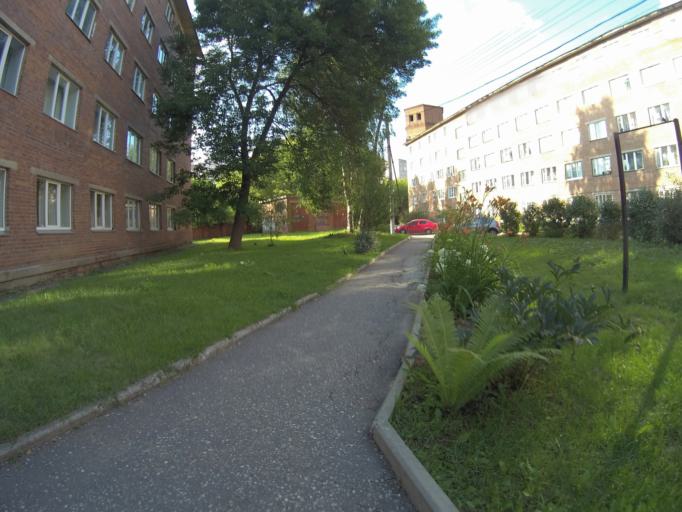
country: RU
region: Vladimir
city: Vladimir
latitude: 56.1407
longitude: 40.3820
